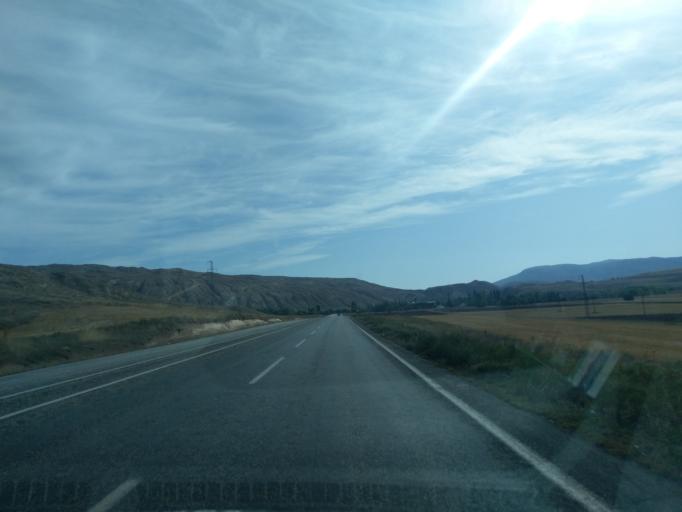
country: TR
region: Sivas
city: Zara
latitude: 39.8619
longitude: 37.8108
